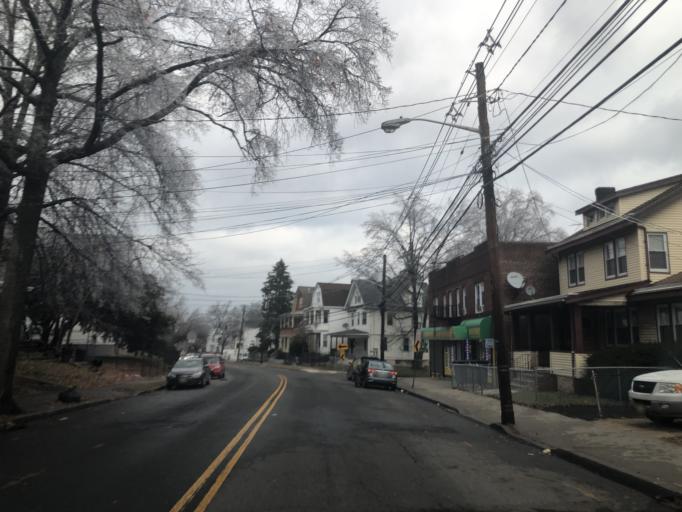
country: US
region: New Jersey
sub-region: Essex County
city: Irvington
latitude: 40.7429
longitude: -74.2327
